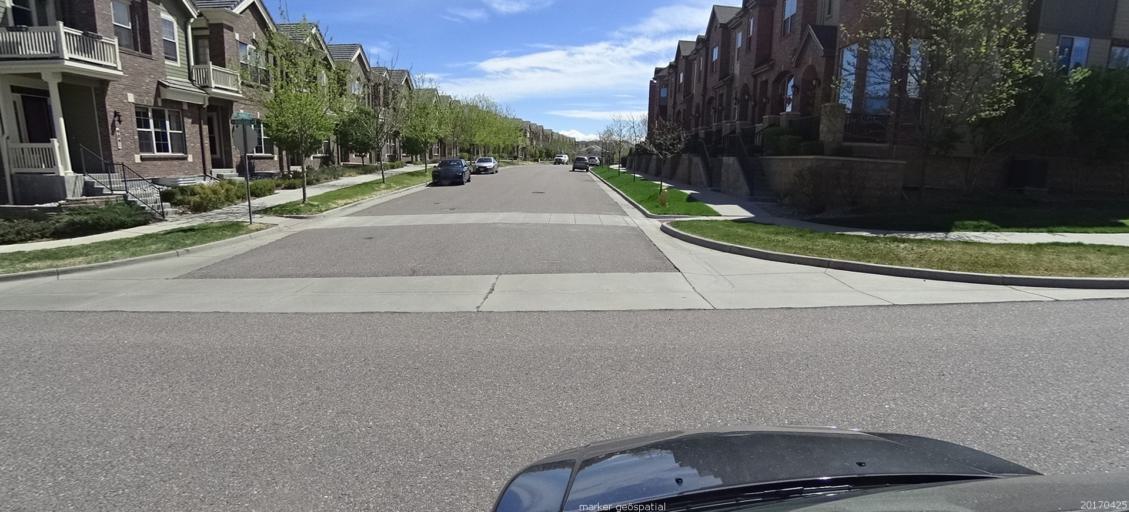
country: US
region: Colorado
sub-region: Douglas County
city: Carriage Club
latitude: 39.5299
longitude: -104.8837
